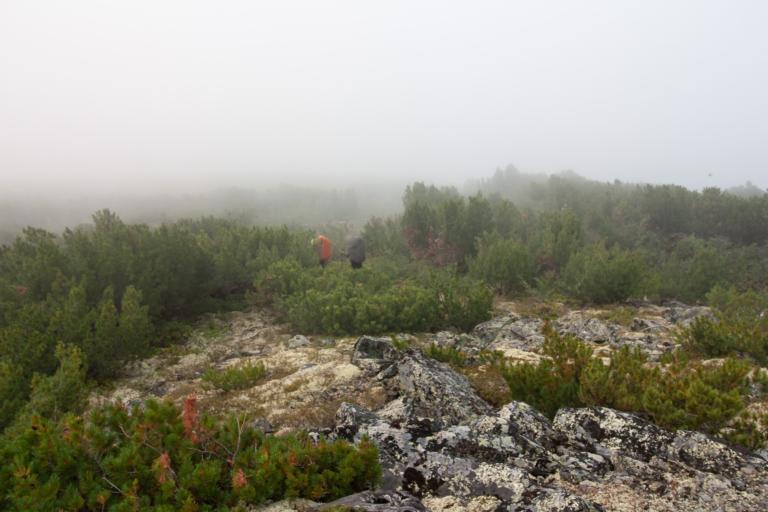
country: RU
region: Respublika Buryatiya
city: Kichera
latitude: 56.3379
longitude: 110.0748
